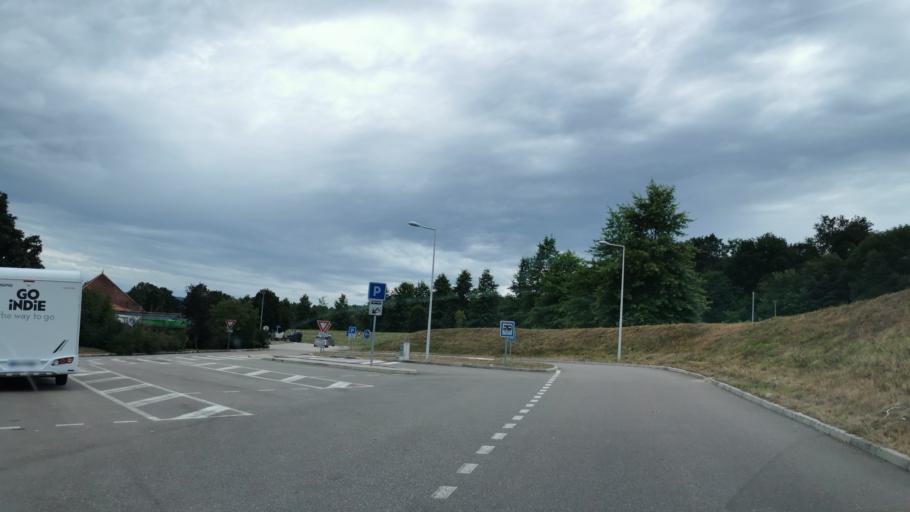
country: FR
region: Bourgogne
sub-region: Departement de Saone-et-Loire
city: Varennes-Saint-Sauveur
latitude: 46.4960
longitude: 5.3104
